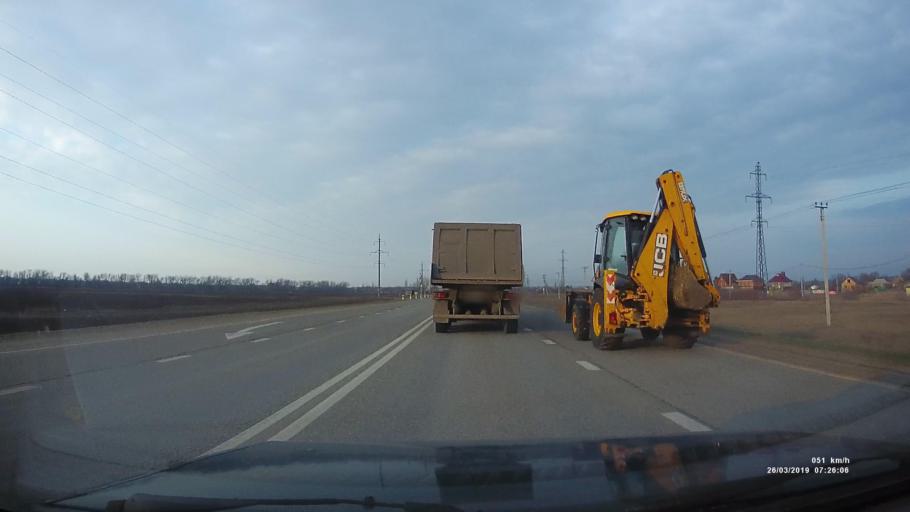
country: RU
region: Rostov
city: Taganrog
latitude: 47.2689
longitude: 38.8439
